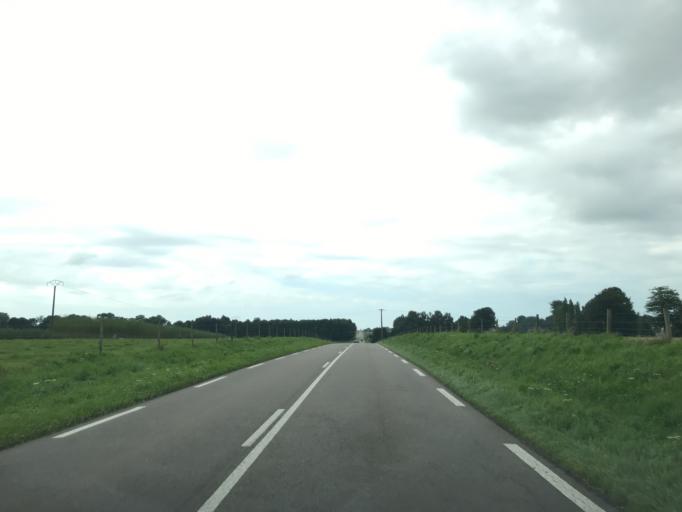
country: FR
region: Haute-Normandie
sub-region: Departement de la Seine-Maritime
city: Breaute
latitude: 49.6306
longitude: 0.3927
